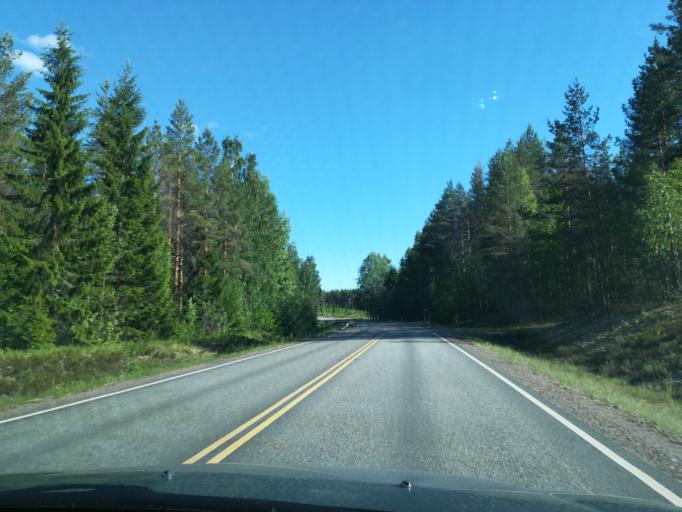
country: FI
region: South Karelia
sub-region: Imatra
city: Ruokolahti
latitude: 61.3946
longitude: 28.6353
